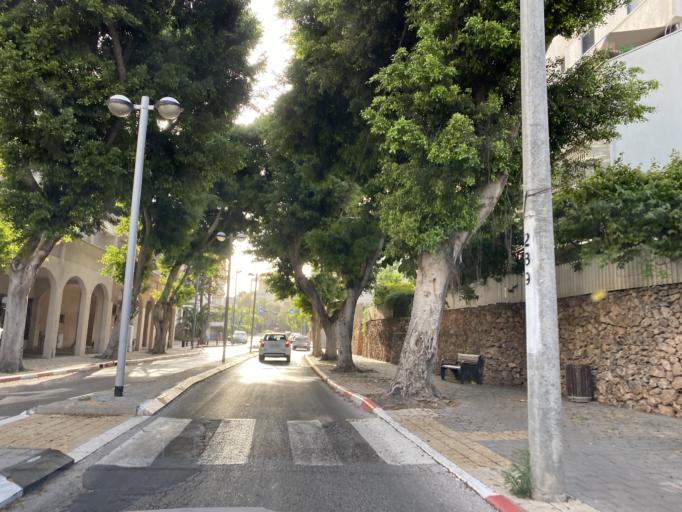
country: IL
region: Central District
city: Kfar Saba
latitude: 32.1786
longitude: 34.9074
